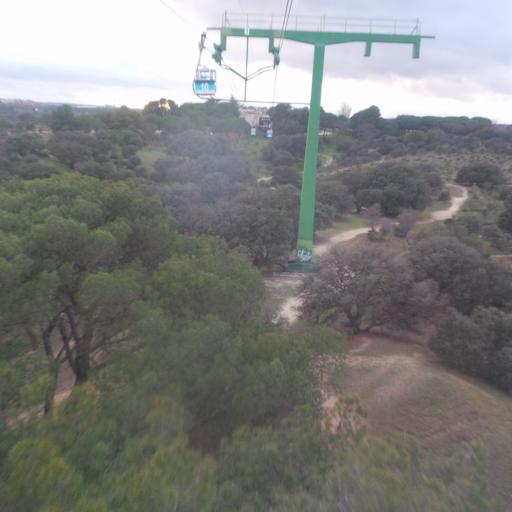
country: ES
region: Madrid
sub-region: Provincia de Madrid
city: Moncloa-Aravaca
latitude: 40.4211
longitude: -3.7444
